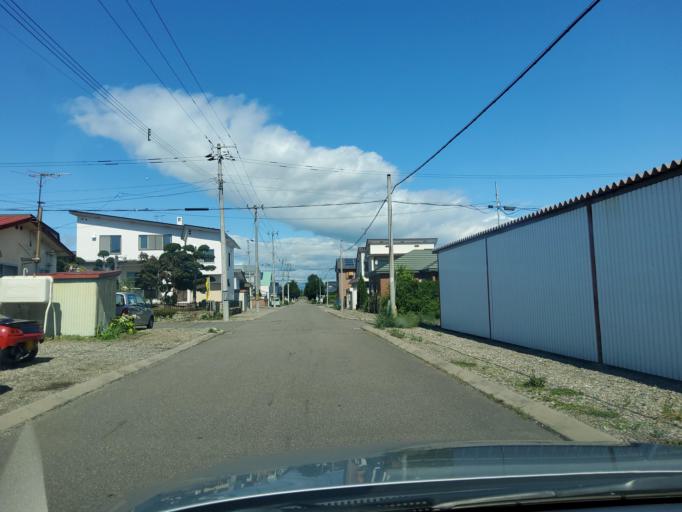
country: JP
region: Hokkaido
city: Otofuke
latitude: 42.9577
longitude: 143.1921
